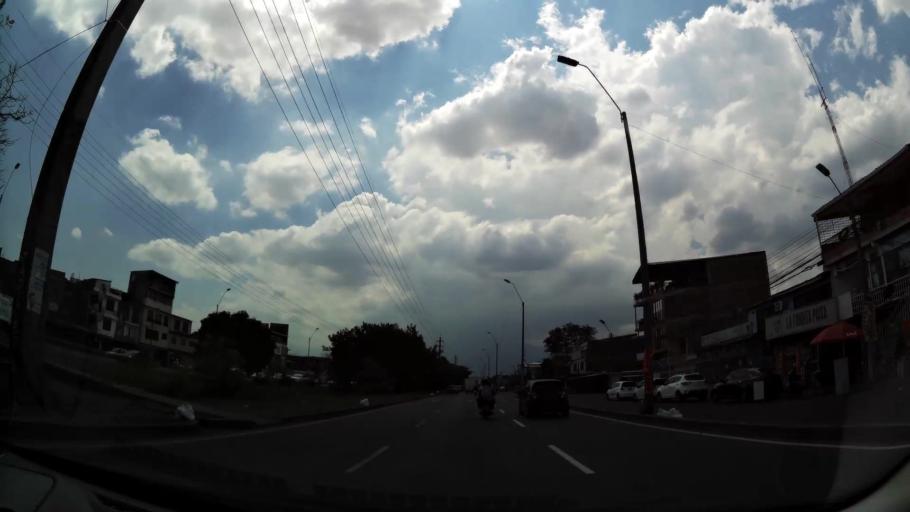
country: CO
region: Valle del Cauca
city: Cali
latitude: 3.4418
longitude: -76.4972
